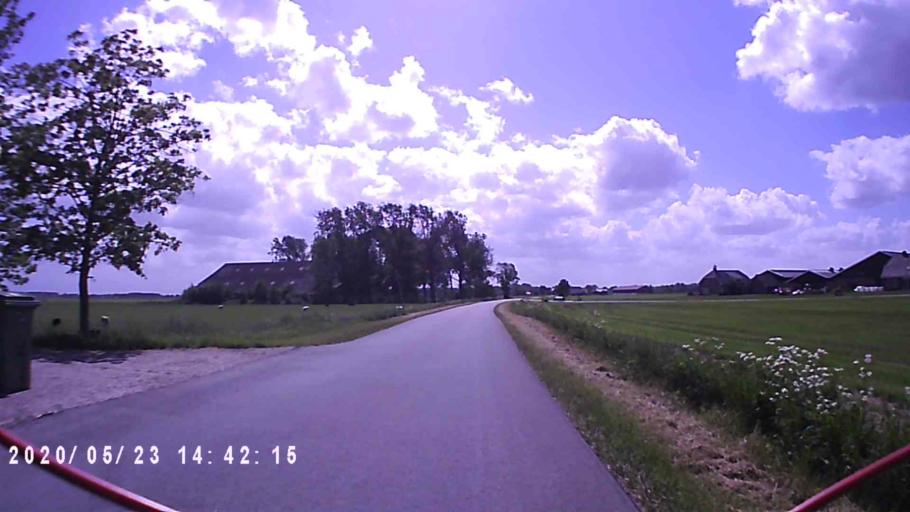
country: NL
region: Groningen
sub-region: Gemeente Delfzijl
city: Delfzijl
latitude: 53.2717
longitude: 6.9627
